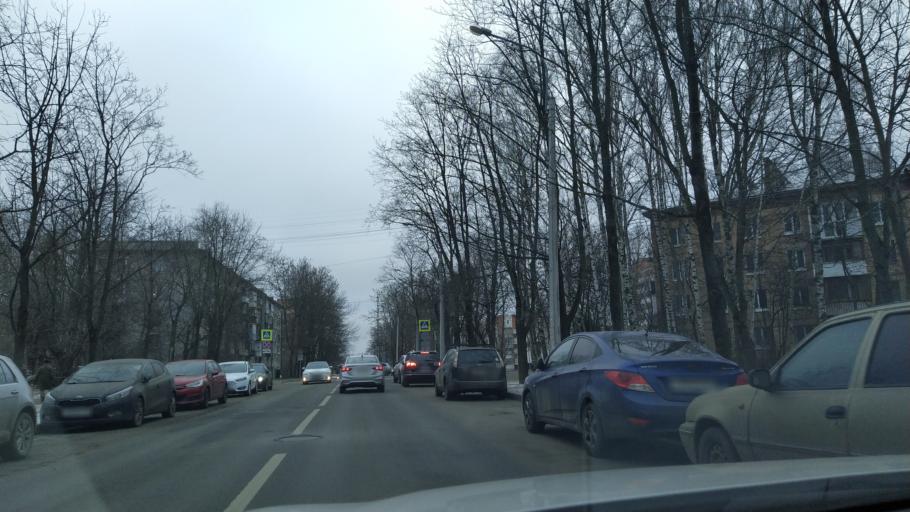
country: RU
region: St.-Petersburg
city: Pushkin
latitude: 59.7277
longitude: 30.4189
